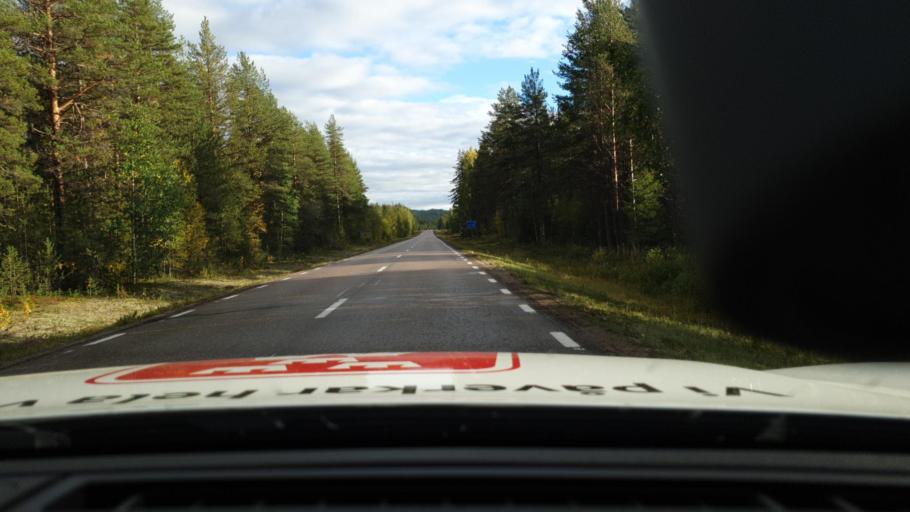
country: SE
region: Norrbotten
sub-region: Overkalix Kommun
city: OEverkalix
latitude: 66.6168
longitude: 22.7516
